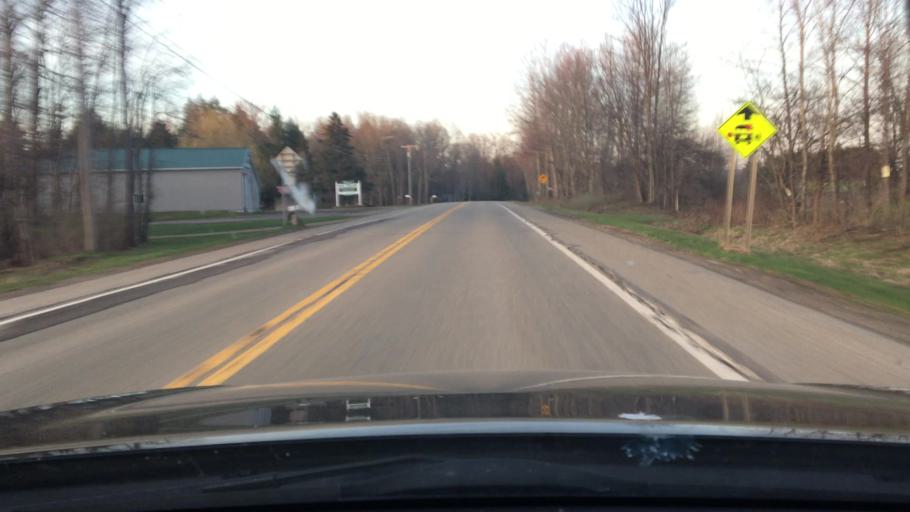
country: US
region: New York
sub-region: Cattaraugus County
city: Randolph
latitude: 42.1875
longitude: -78.9156
